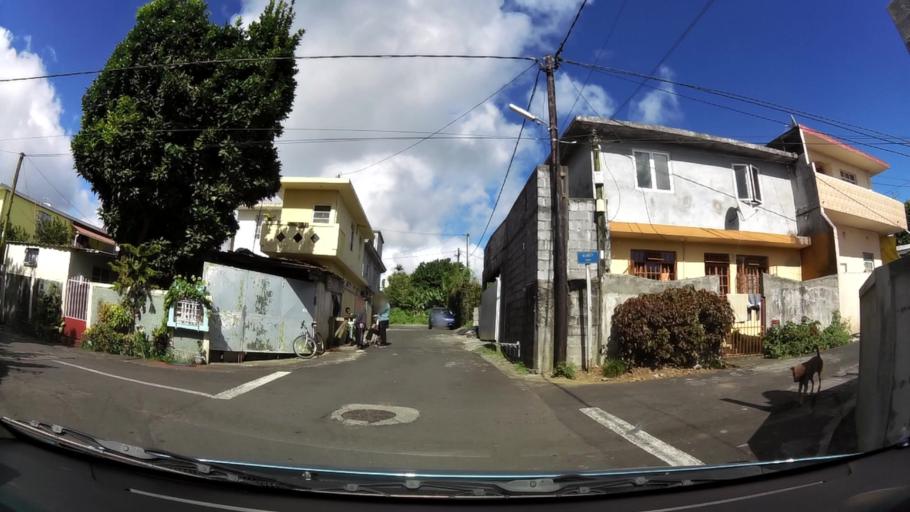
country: MU
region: Plaines Wilhems
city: Curepipe
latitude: -20.3300
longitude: 57.5202
